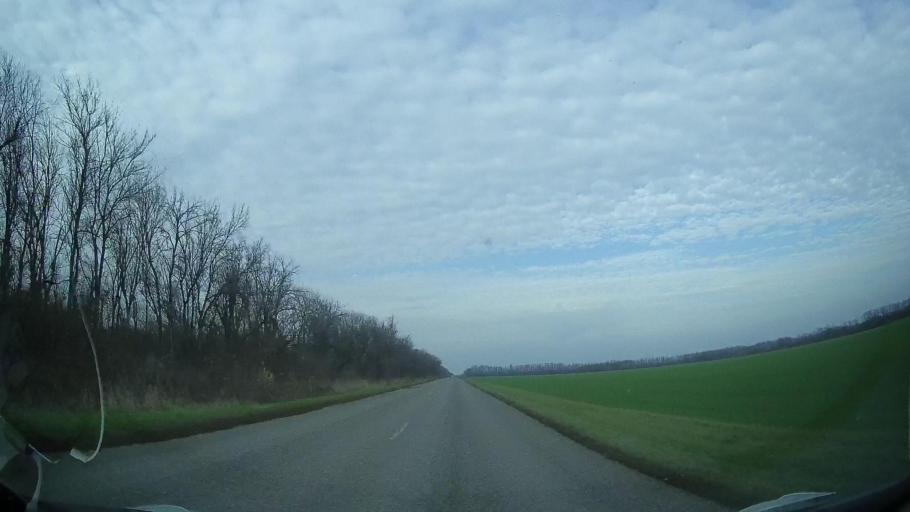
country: RU
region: Rostov
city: Zernograd
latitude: 46.9797
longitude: 40.3916
